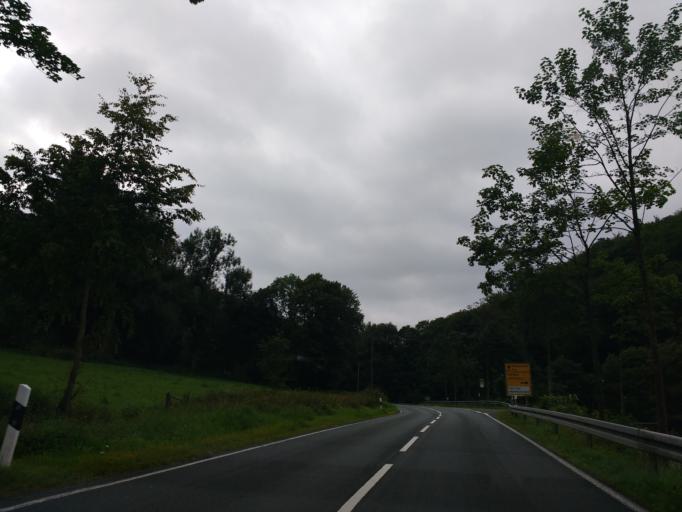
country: DE
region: North Rhine-Westphalia
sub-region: Regierungsbezirk Arnsberg
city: Olsberg
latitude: 51.3240
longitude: 8.4494
